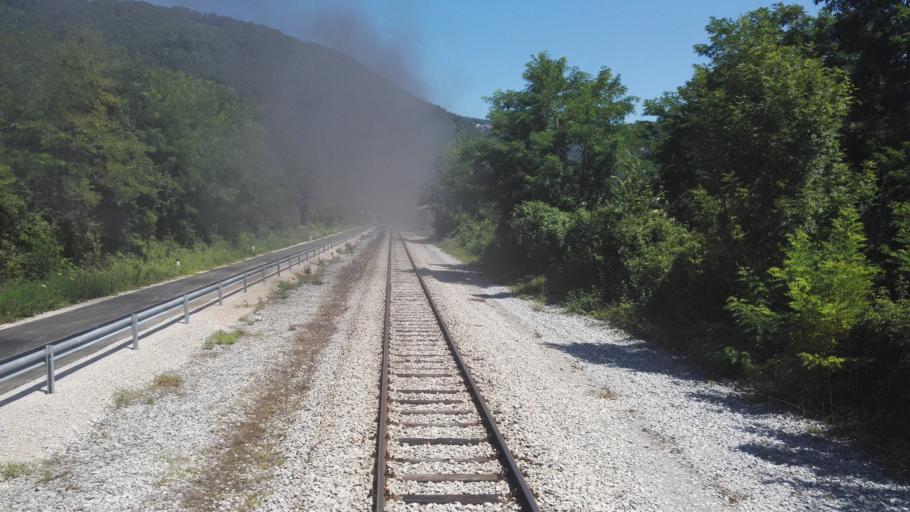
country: SI
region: Kanal
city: Deskle
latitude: 46.0442
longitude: 13.5888
